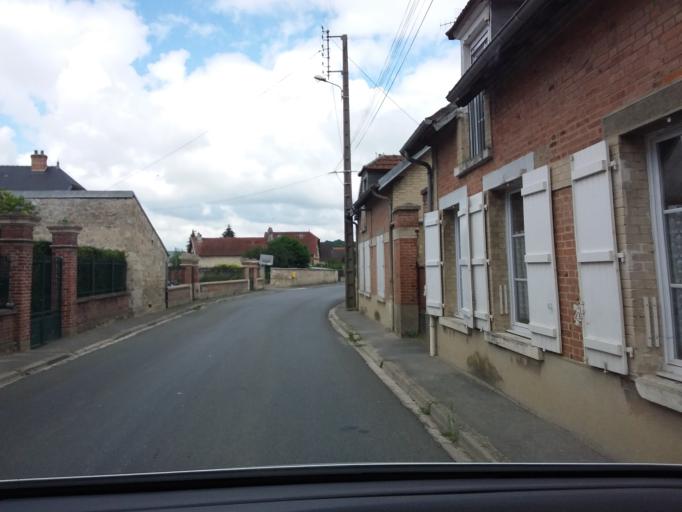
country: FR
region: Picardie
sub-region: Departement de l'Aisne
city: Vailly-sur-Aisne
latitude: 49.4085
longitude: 3.5232
